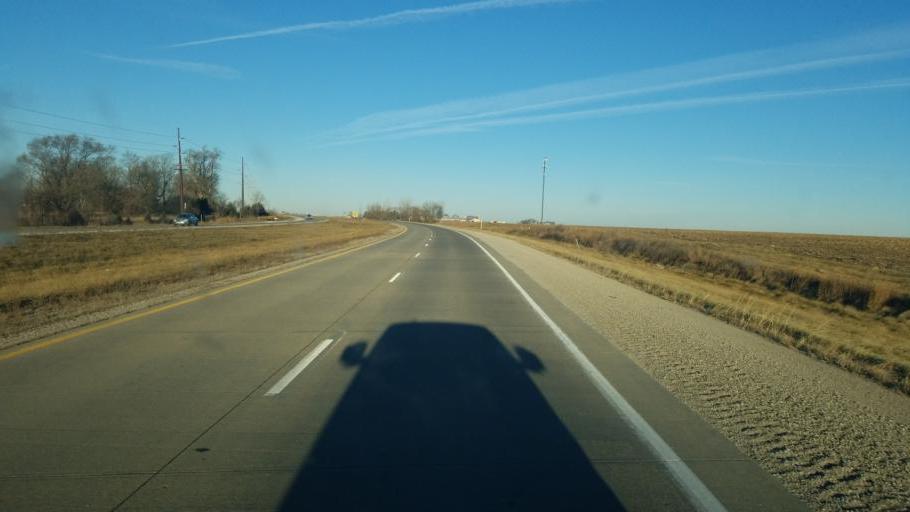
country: US
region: Iowa
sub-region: Mahaska County
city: Oskaloosa
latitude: 41.3532
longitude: -92.7601
